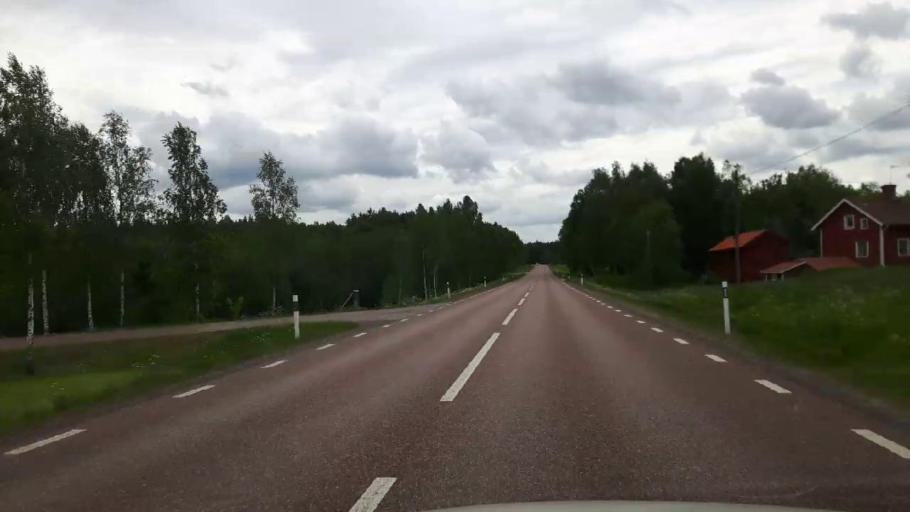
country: SE
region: Dalarna
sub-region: Hedemora Kommun
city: Brunna
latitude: 60.2134
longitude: 15.9918
